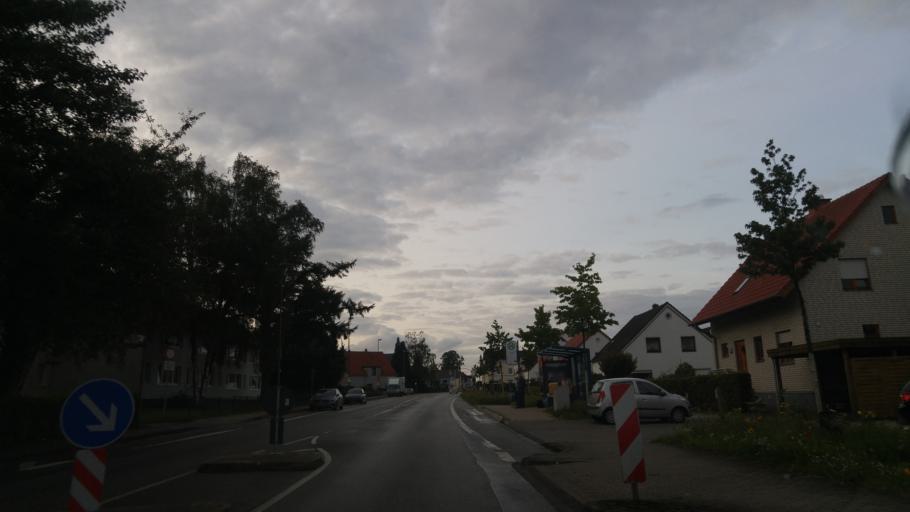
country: DE
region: North Rhine-Westphalia
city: Spenge
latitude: 52.0926
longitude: 8.5145
